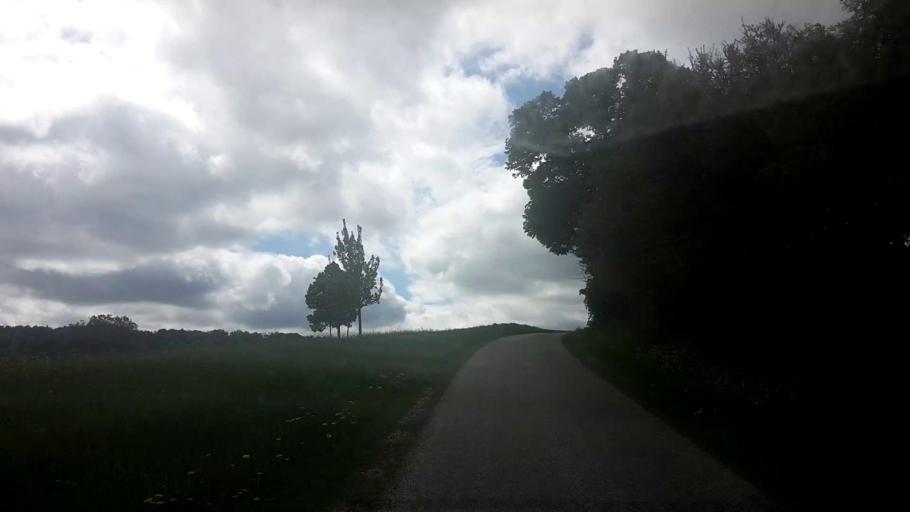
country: DE
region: Bavaria
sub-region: Upper Franconia
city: Bad Staffelstein
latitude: 50.1056
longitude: 11.0366
